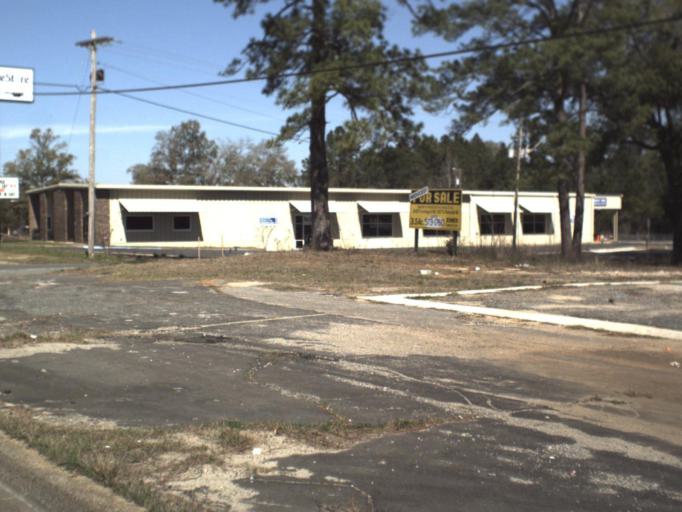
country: US
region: Florida
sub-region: Jackson County
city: Marianna
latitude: 30.7625
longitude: -85.2000
